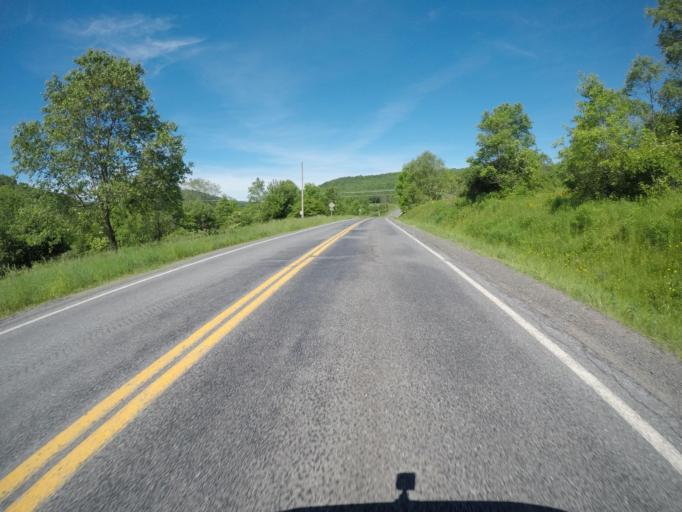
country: US
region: New York
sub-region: Delaware County
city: Delhi
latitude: 42.2148
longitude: -74.8986
